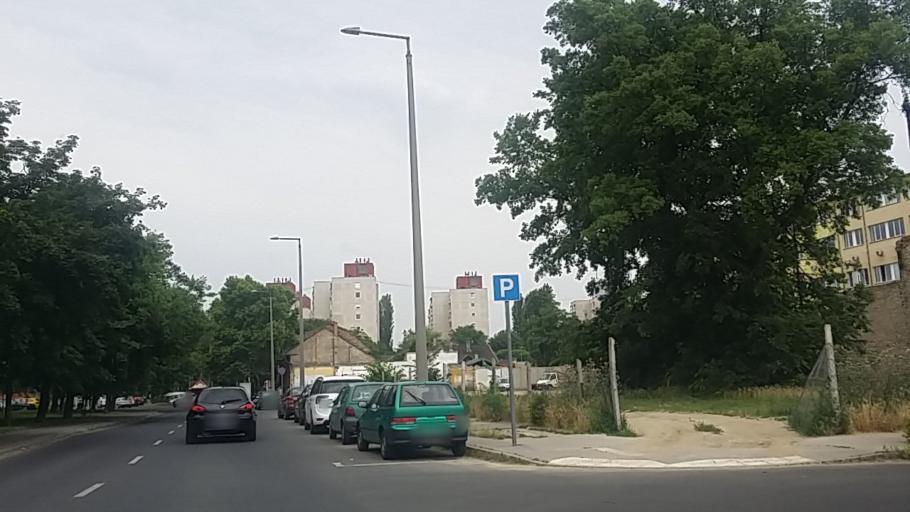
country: HU
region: Budapest
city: Budapest XIX. keruelet
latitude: 47.4608
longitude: 19.1417
